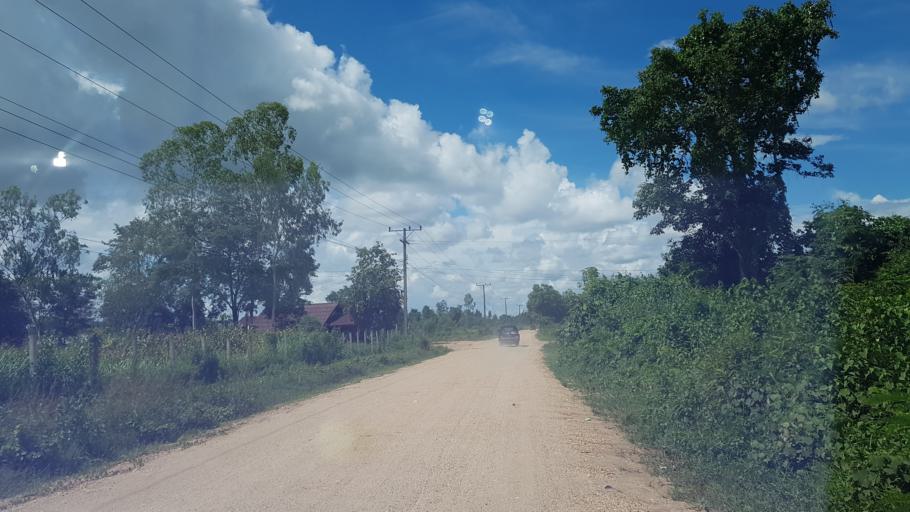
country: LA
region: Vientiane
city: Vientiane
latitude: 18.2290
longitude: 102.5248
